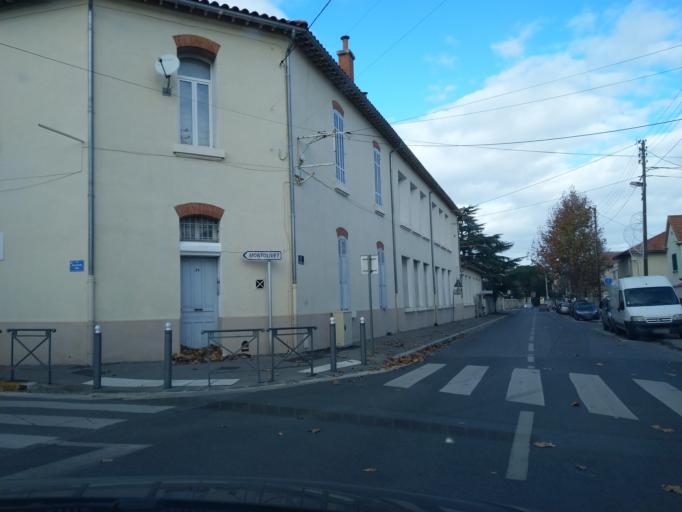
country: FR
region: Provence-Alpes-Cote d'Azur
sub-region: Departement des Bouches-du-Rhone
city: Marseille 13
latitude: 43.3177
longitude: 5.4282
